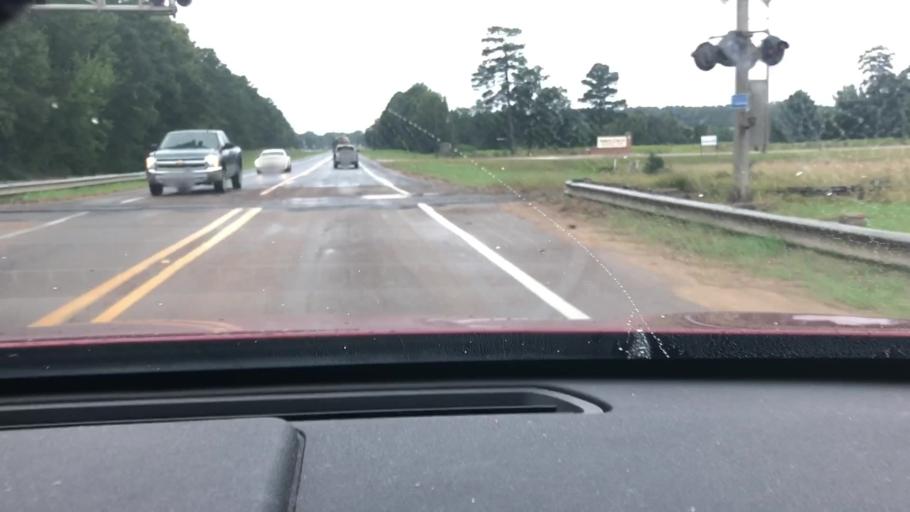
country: US
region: Arkansas
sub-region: Columbia County
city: Magnolia
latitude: 33.2970
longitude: -93.2423
